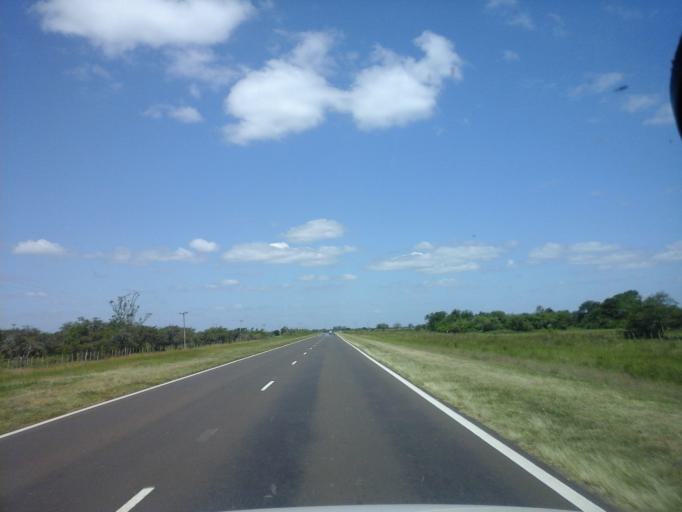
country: PY
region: Neembucu
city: Cerrito
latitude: -27.3406
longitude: -57.9028
